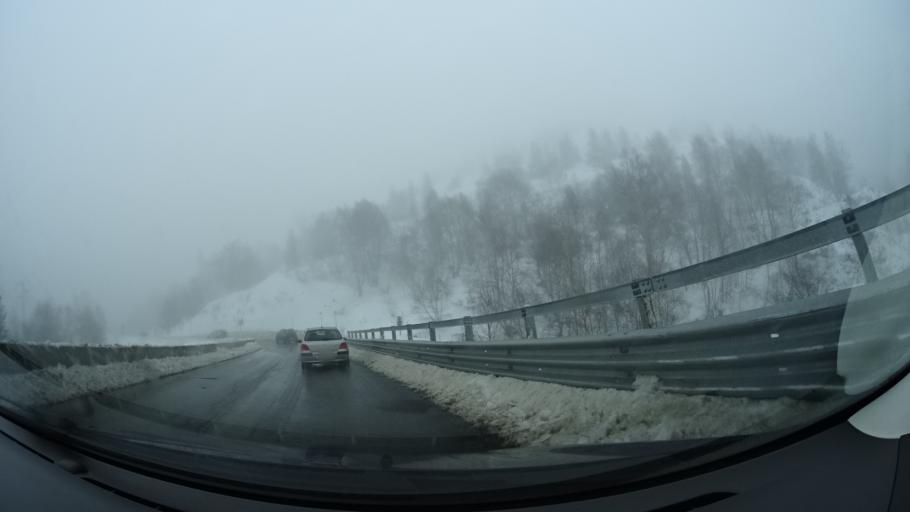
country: AD
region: Encamp
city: Pas de la Casa
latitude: 42.5717
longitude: 1.7881
